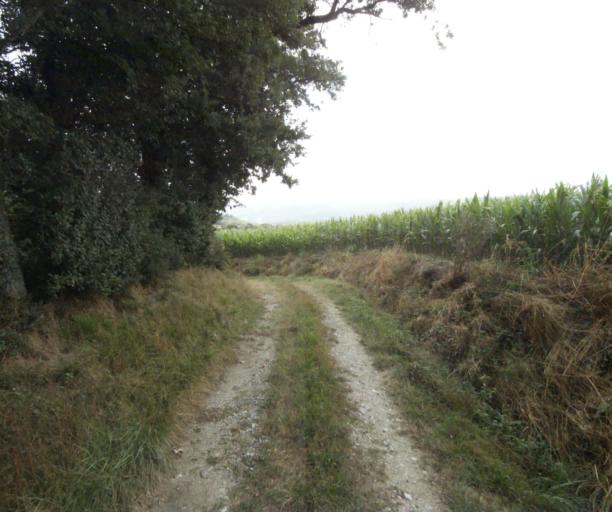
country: FR
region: Midi-Pyrenees
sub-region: Departement du Tarn
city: Soreze
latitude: 43.4871
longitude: 2.0887
